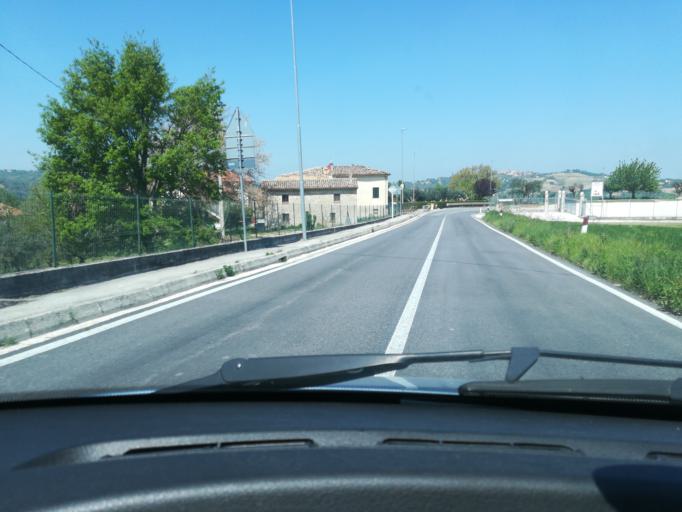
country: IT
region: The Marches
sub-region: Provincia di Macerata
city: Strada
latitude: 43.3946
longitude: 13.2059
